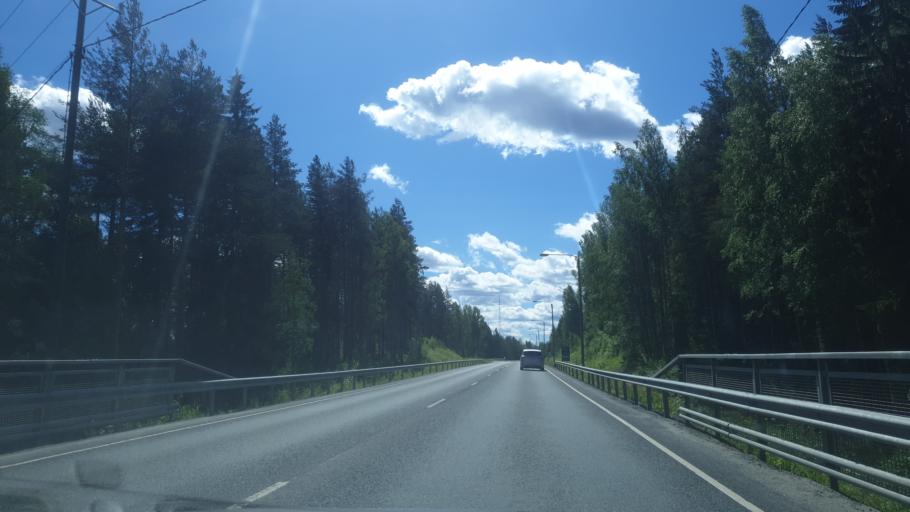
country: FI
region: Northern Savo
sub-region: Varkaus
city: Leppaevirta
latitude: 62.5885
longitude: 27.6051
